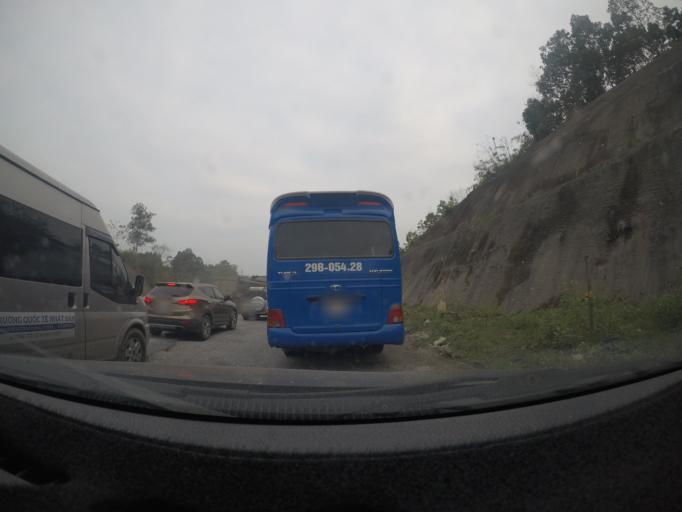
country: VN
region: Yen Bai
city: Co Phuc
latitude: 21.7911
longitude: 104.7658
